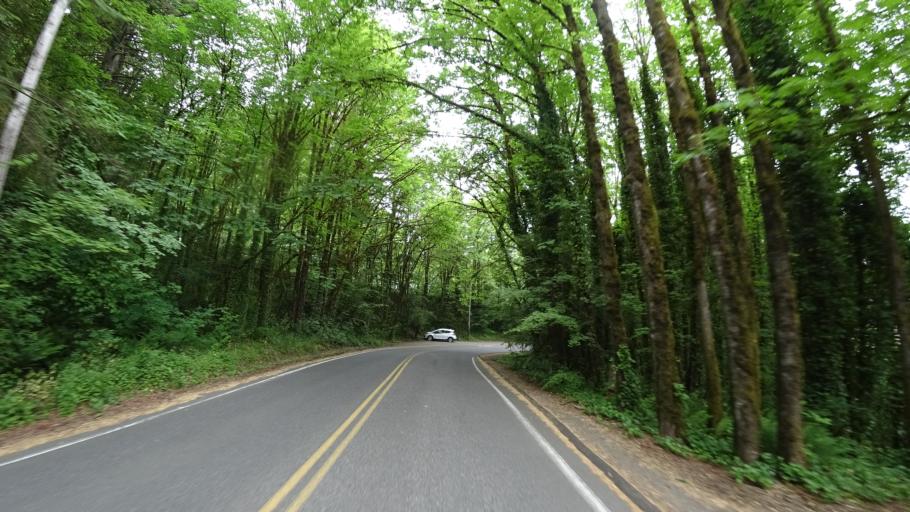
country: US
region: Oregon
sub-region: Multnomah County
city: Portland
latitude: 45.5006
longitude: -122.7065
